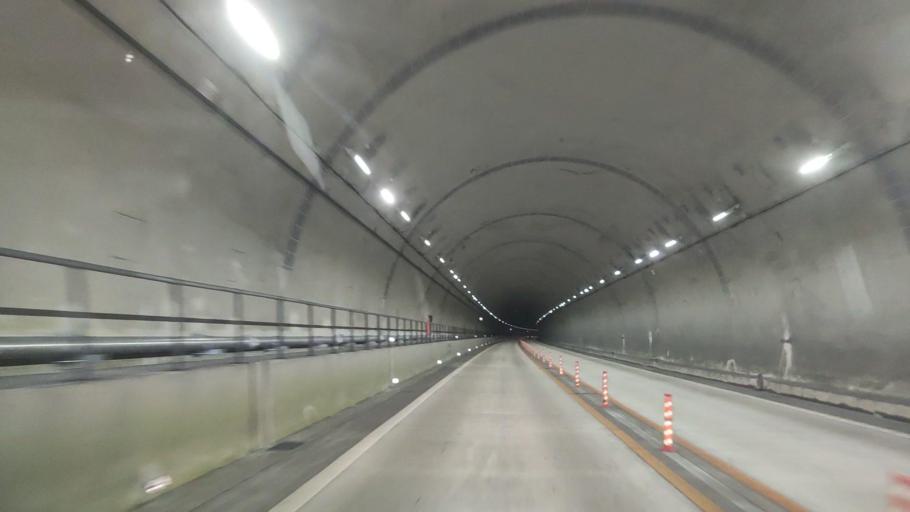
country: JP
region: Ehime
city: Hojo
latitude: 34.0780
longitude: 132.9760
